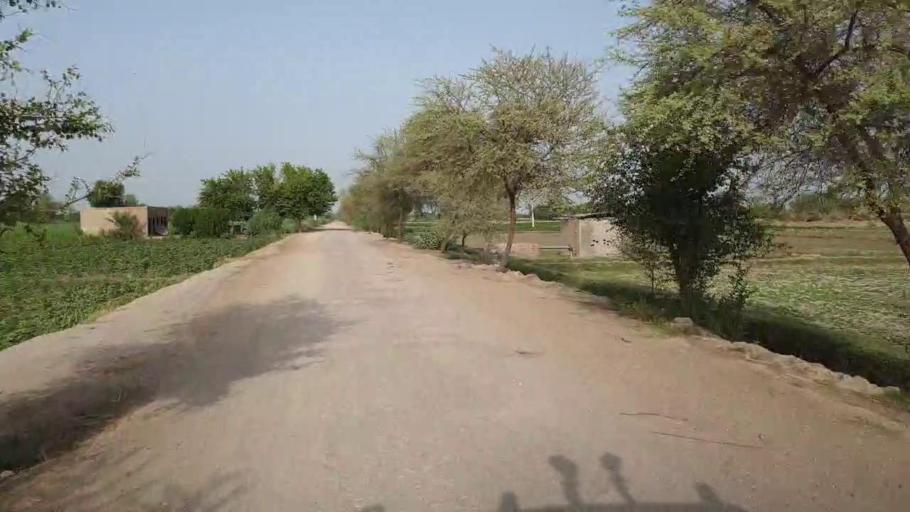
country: PK
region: Sindh
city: Daur
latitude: 26.3432
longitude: 68.2637
